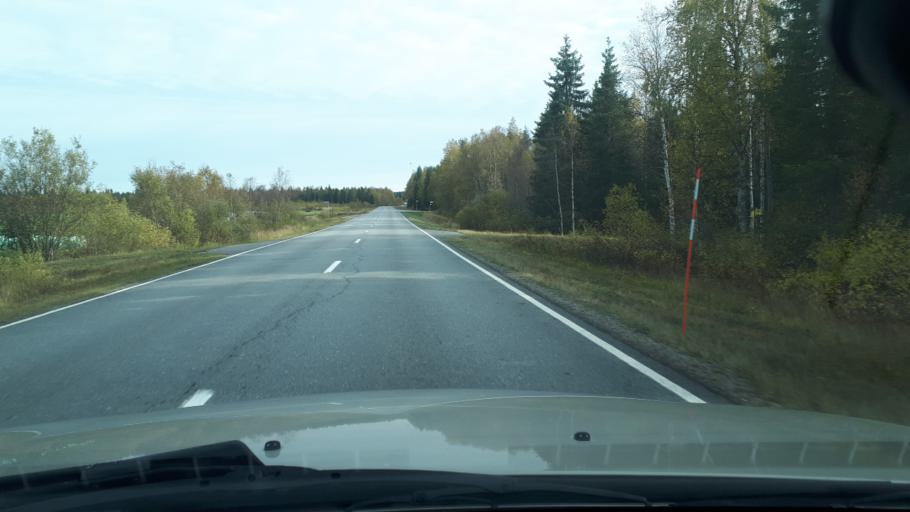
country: FI
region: Lapland
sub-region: Rovaniemi
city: Ranua
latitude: 65.9821
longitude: 26.1453
